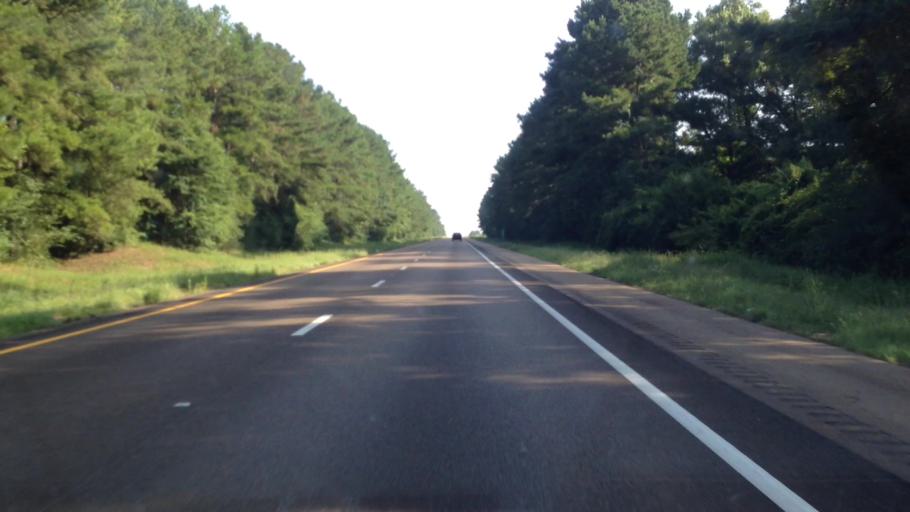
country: US
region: Mississippi
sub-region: Pike County
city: Summit
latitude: 31.3607
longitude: -90.4791
